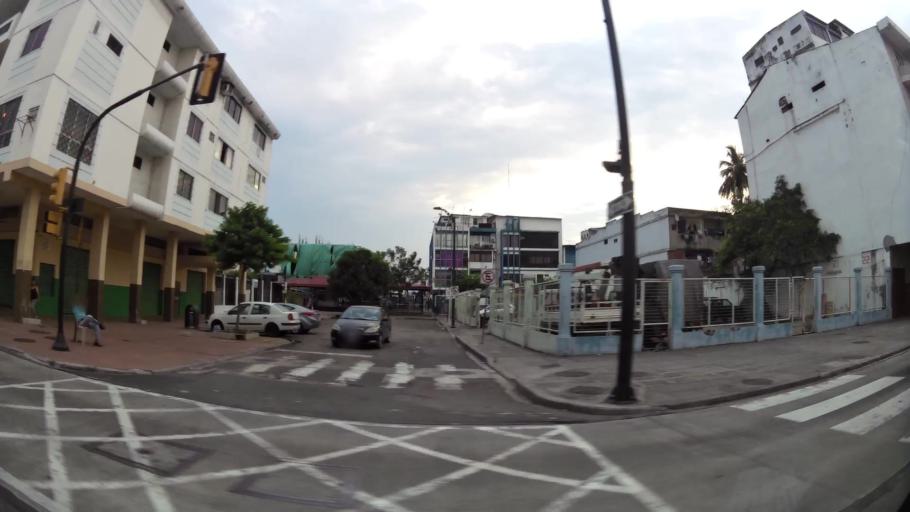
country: EC
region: Guayas
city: Guayaquil
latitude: -2.2039
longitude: -79.8844
